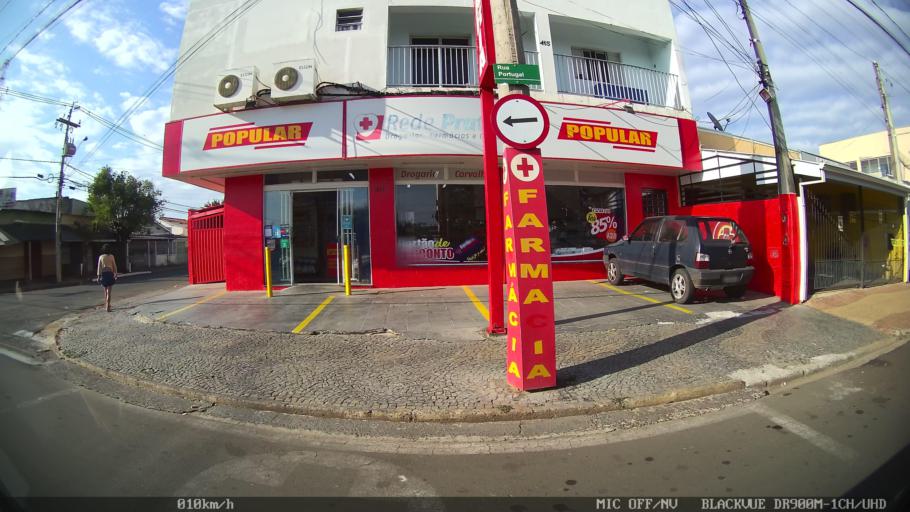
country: BR
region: Sao Paulo
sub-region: Americana
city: Americana
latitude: -22.7235
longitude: -47.3672
